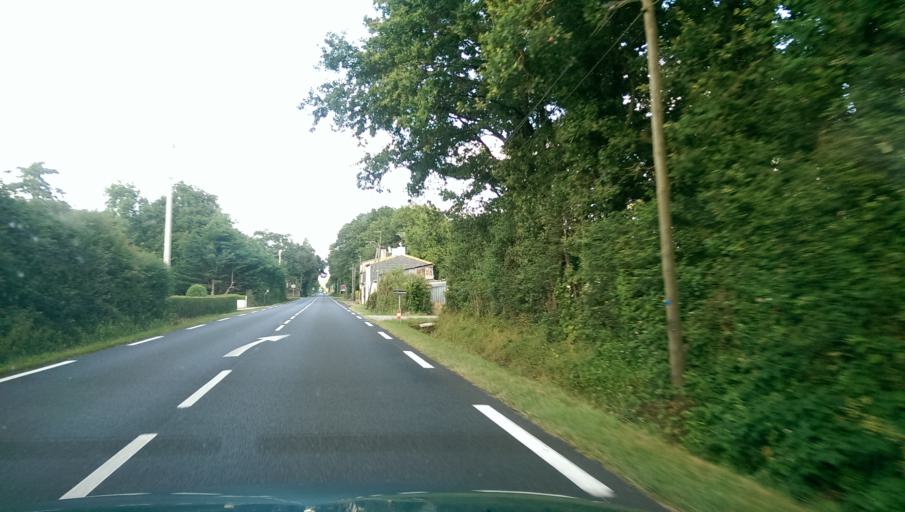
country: FR
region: Pays de la Loire
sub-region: Departement de la Vendee
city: Rocheserviere
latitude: 46.9243
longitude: -1.5307
